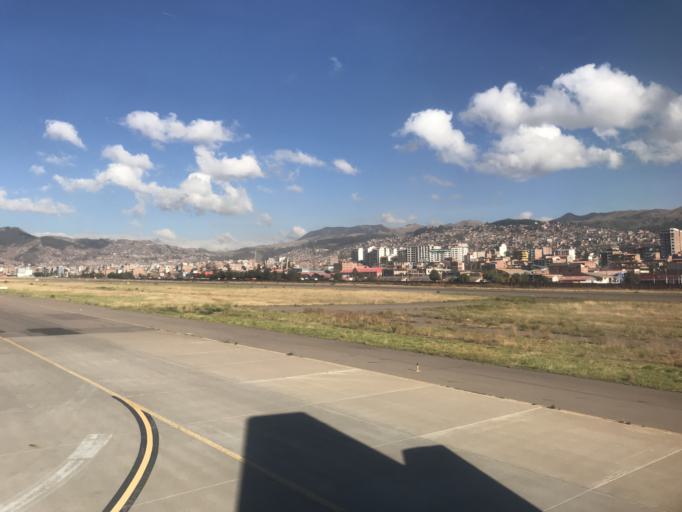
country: PE
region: Cusco
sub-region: Provincia de Cusco
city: Cusco
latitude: -13.5364
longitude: -71.9445
